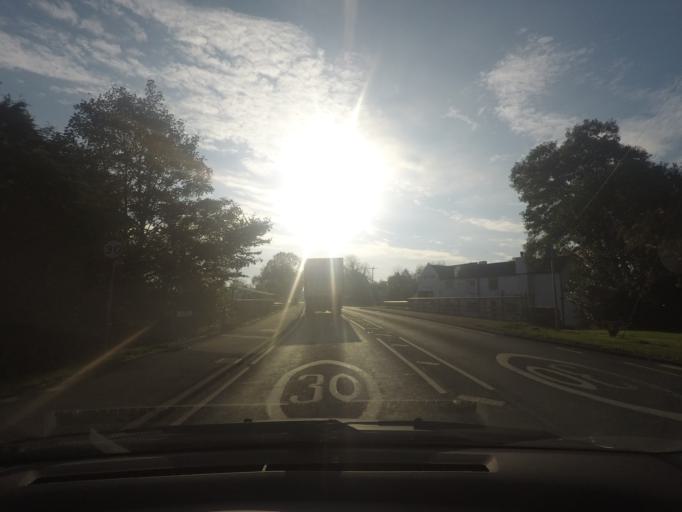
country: GB
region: England
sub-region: East Riding of Yorkshire
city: Londesborough
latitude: 53.8768
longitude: -0.7047
